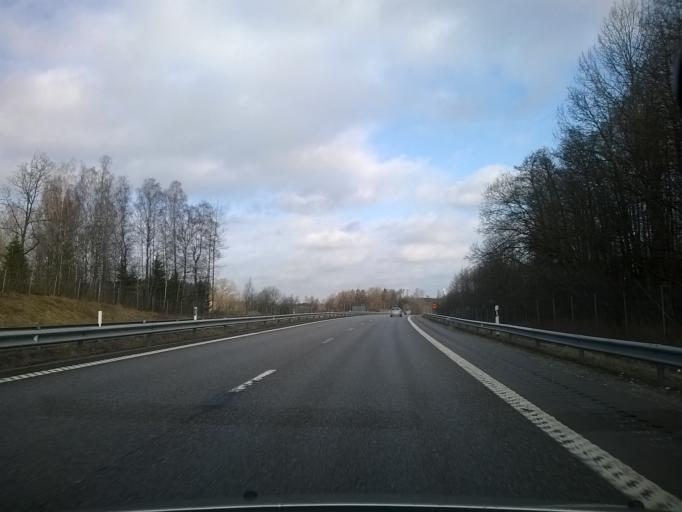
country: SE
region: Vaestra Goetaland
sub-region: Uddevalla Kommun
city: Ljungskile
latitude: 58.2967
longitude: 11.8626
